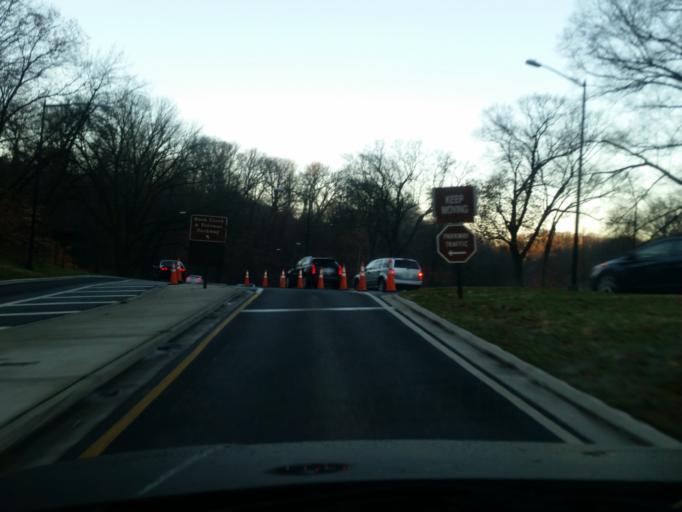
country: US
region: Washington, D.C.
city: Washington, D.C.
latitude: 38.9214
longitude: -77.0509
